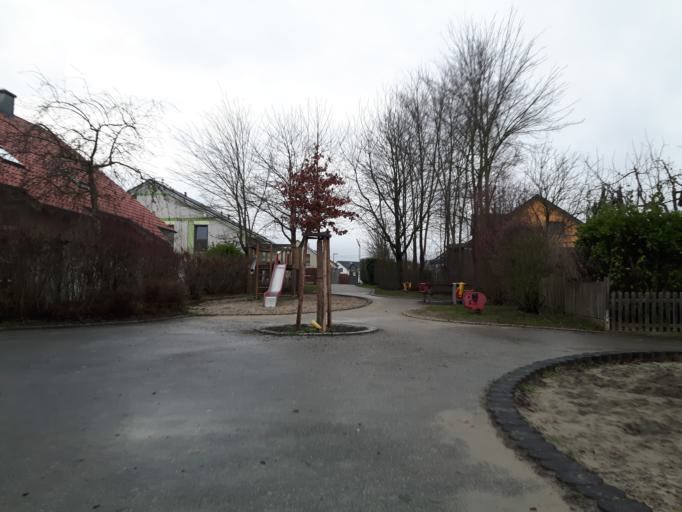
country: DE
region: Baden-Wuerttemberg
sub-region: Regierungsbezirk Stuttgart
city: Nordheim
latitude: 49.1046
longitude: 9.1250
